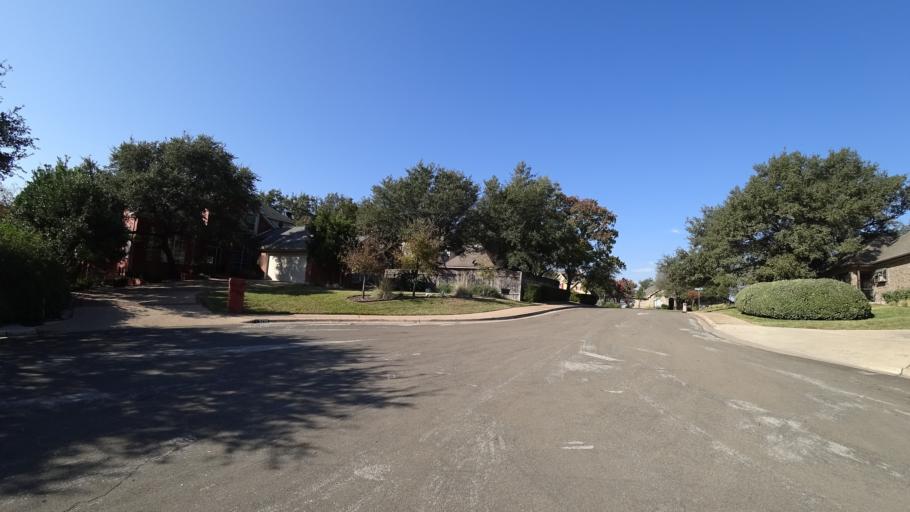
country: US
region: Texas
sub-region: Williamson County
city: Jollyville
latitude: 30.3947
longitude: -97.7680
